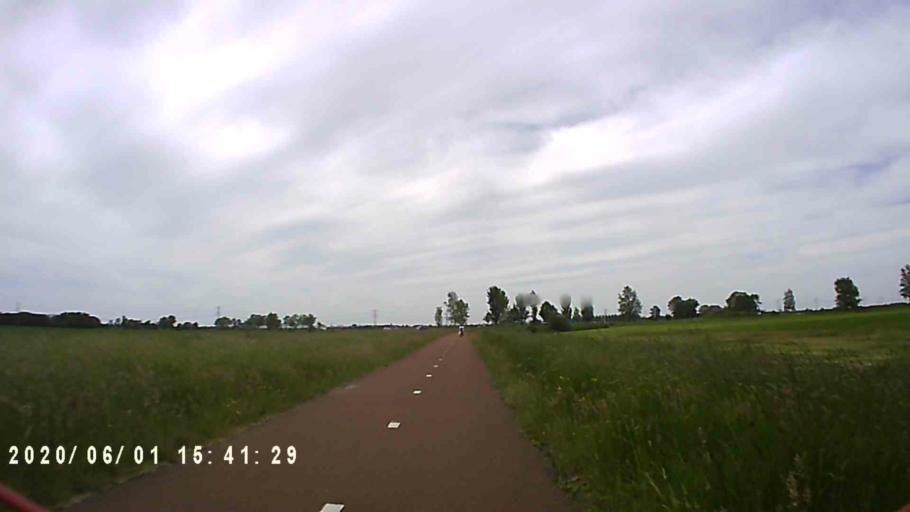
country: NL
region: Friesland
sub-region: Gemeente Boarnsterhim
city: Wergea
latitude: 53.1562
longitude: 5.8248
